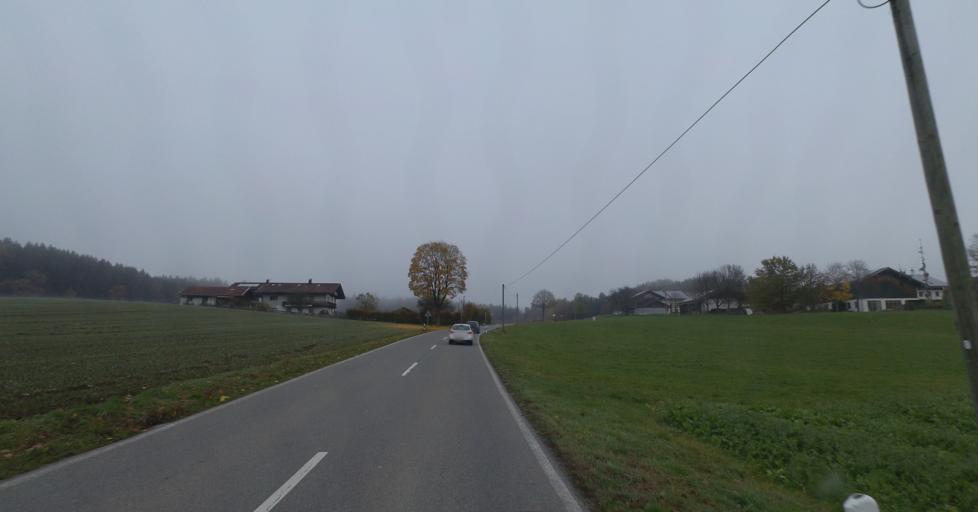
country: DE
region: Bavaria
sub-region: Upper Bavaria
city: Seeon-Seebruck
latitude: 47.9657
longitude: 12.5216
